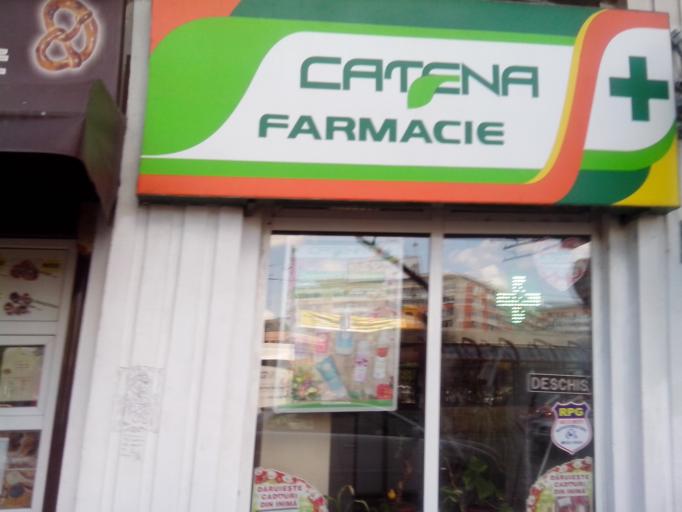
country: RO
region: Bucuresti
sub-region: Municipiul Bucuresti
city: Bucharest
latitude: 44.4410
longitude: 26.1334
